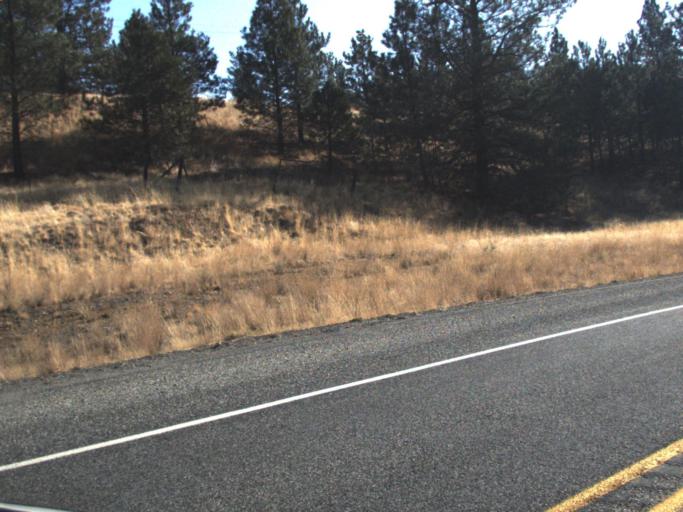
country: US
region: Washington
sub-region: Ferry County
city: Republic
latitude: 48.6621
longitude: -118.6656
